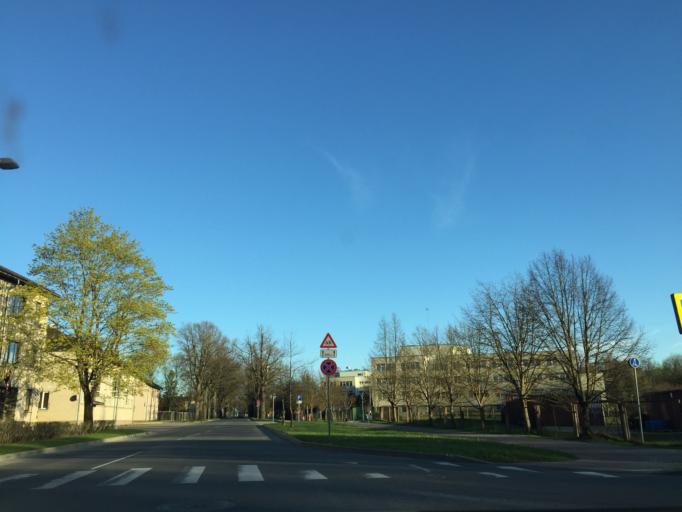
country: LV
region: Valmieras Rajons
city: Valmiera
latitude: 57.5477
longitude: 25.4222
